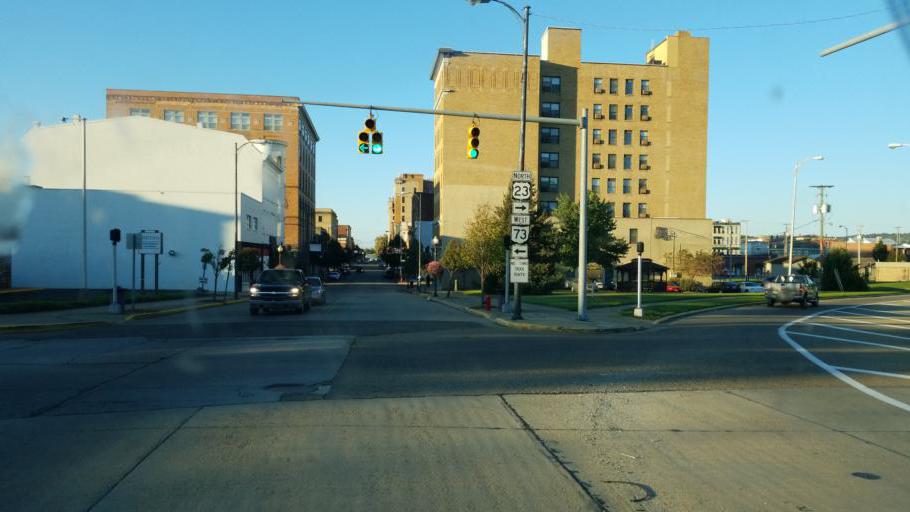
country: US
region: Ohio
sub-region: Scioto County
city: Portsmouth
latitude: 38.7314
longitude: -82.9967
